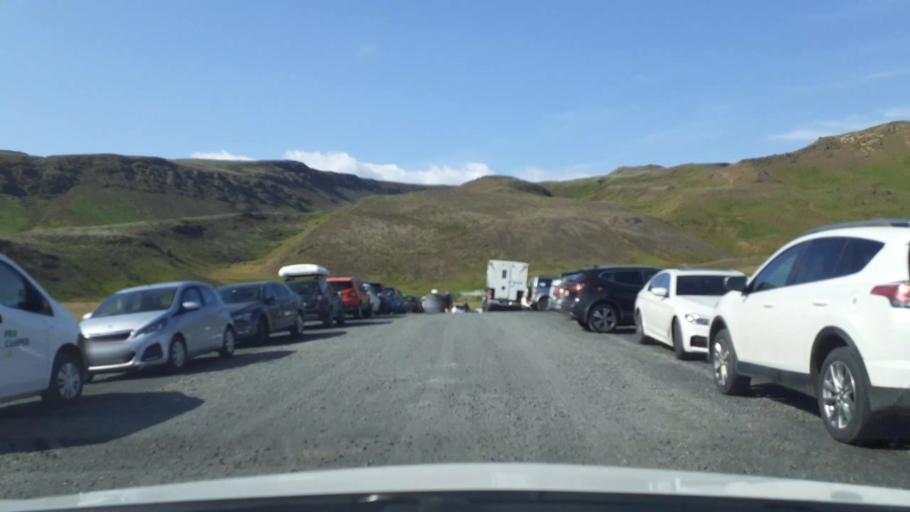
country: IS
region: South
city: Hveragerdi
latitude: 64.0212
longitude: -21.2101
